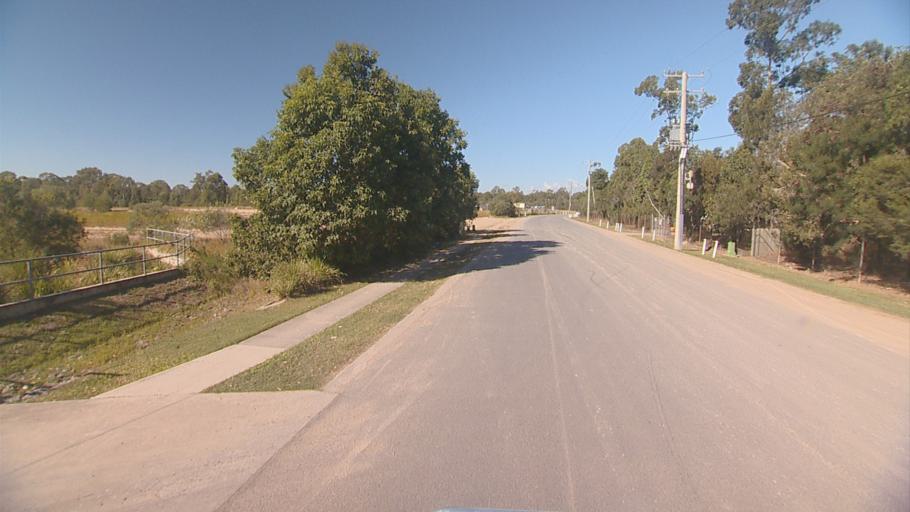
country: AU
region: Queensland
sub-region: Logan
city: Waterford West
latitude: -27.6714
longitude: 153.1162
